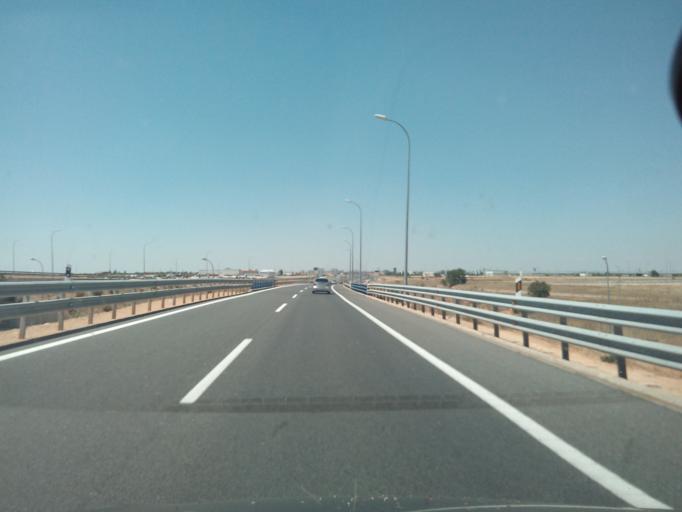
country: ES
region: Castille-La Mancha
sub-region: Province of Toledo
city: Ocana
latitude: 39.9227
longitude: -3.4807
